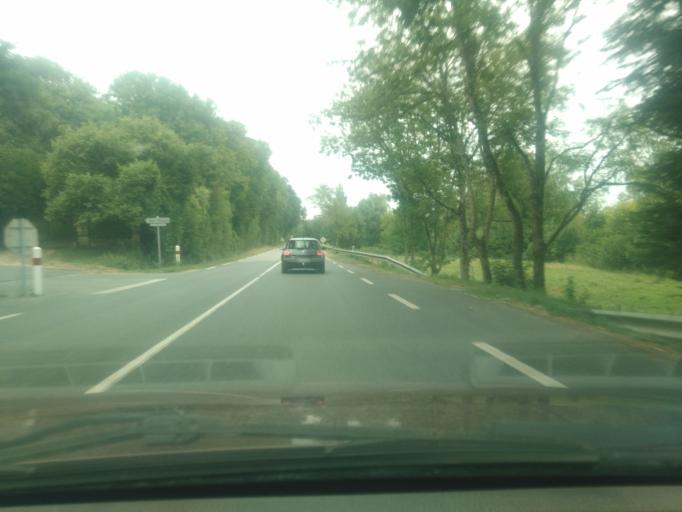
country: FR
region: Centre
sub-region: Departement de l'Indre
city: Le Blanc
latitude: 46.6325
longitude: 1.1011
